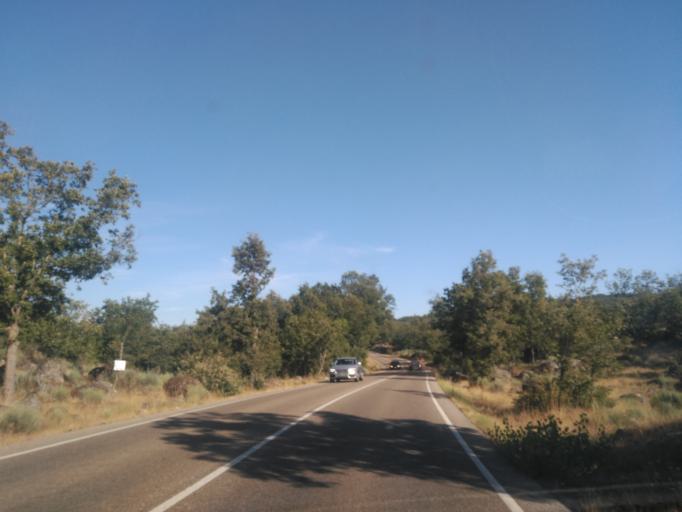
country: ES
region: Castille and Leon
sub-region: Provincia de Zamora
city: Galende
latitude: 42.1133
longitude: -6.6821
